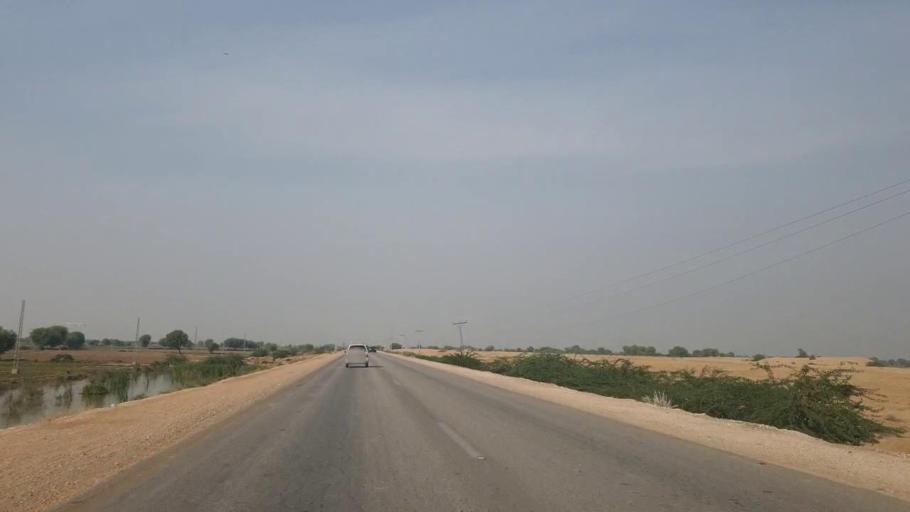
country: PK
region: Sindh
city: Sann
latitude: 26.0648
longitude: 68.1018
